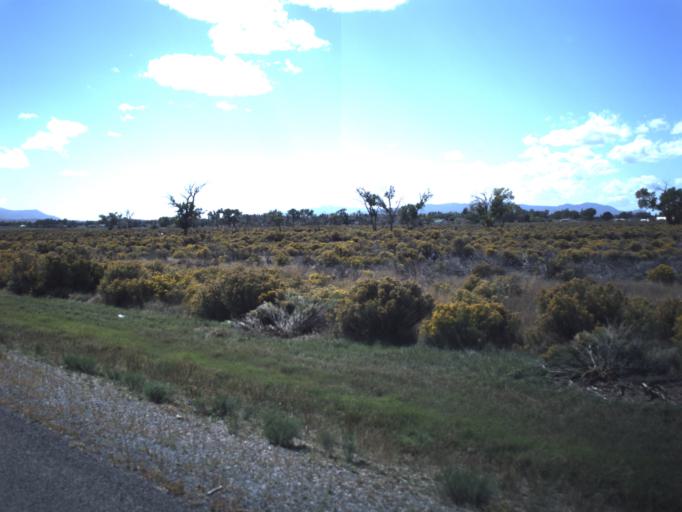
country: US
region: Utah
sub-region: Iron County
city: Enoch
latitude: 37.7625
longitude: -113.0553
